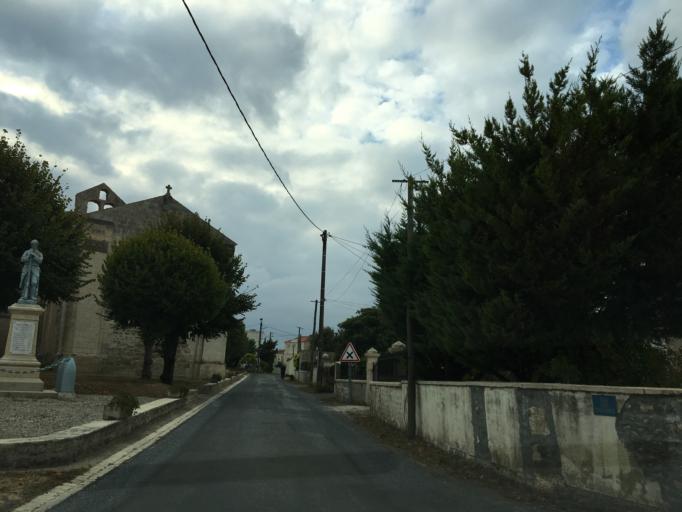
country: FR
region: Poitou-Charentes
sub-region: Departement des Deux-Sevres
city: Beauvoir-sur-Niort
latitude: 46.0778
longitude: -0.4965
